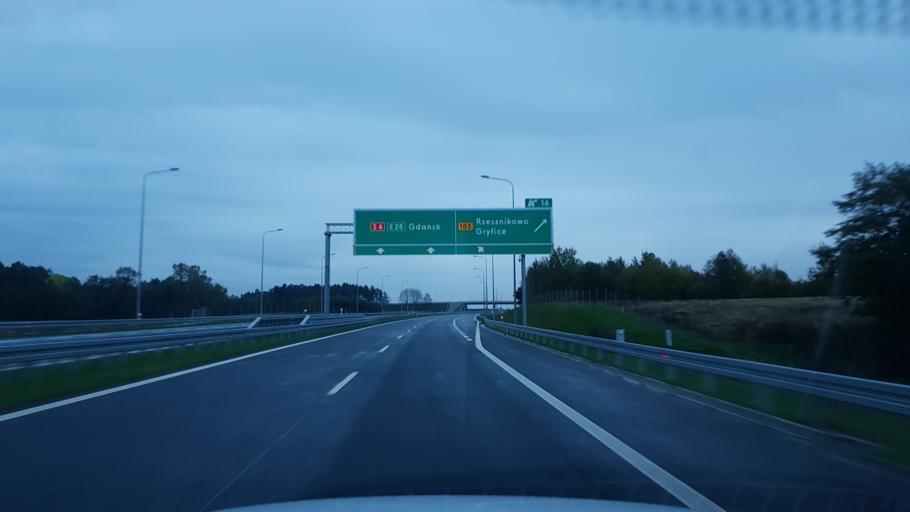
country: PL
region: West Pomeranian Voivodeship
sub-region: Powiat gryficki
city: Brojce
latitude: 53.9390
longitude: 15.3951
